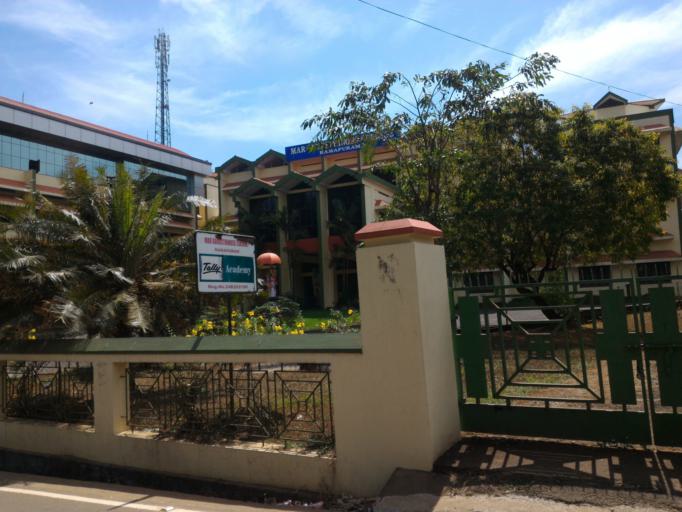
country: IN
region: Kerala
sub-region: Kottayam
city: Palackattumala
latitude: 9.7997
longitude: 76.6637
